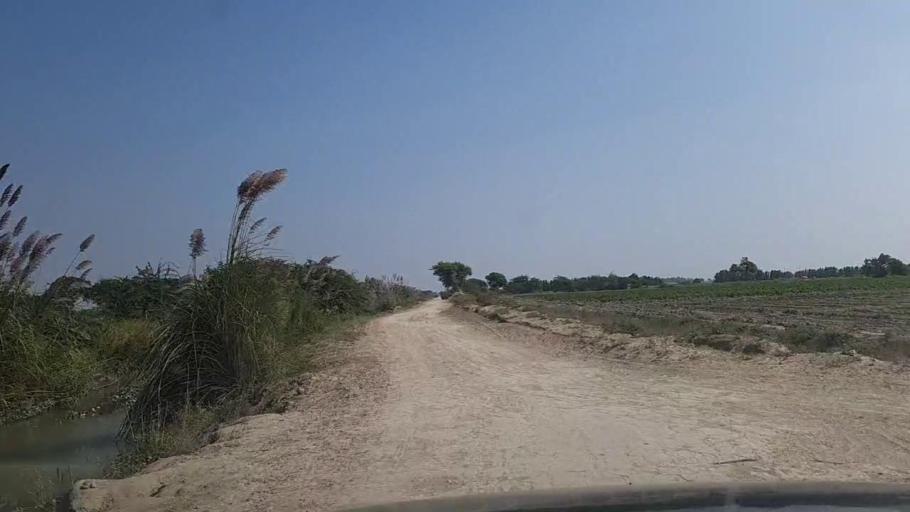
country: PK
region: Sindh
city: Gharo
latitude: 24.7134
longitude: 67.5795
